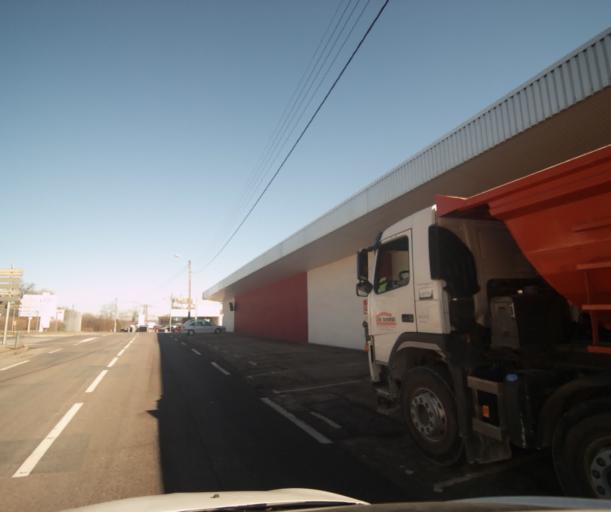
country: FR
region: Franche-Comte
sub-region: Departement du Doubs
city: Thise
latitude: 47.2663
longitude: 6.0530
